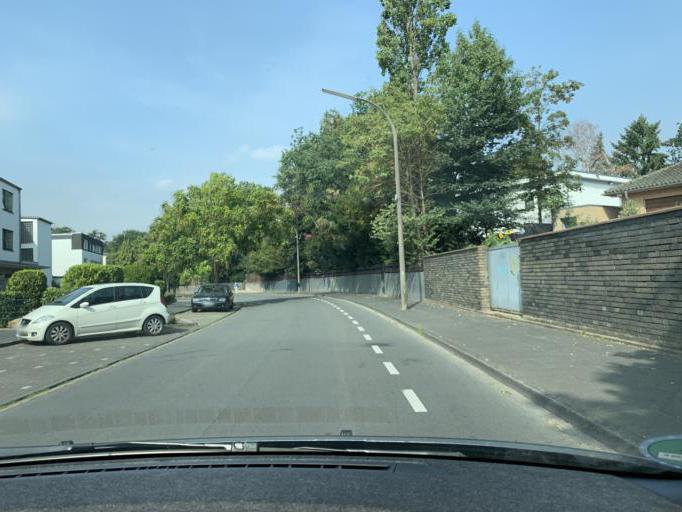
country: DE
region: North Rhine-Westphalia
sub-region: Regierungsbezirk Koln
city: Erftstadt
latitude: 50.8106
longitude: 6.8234
